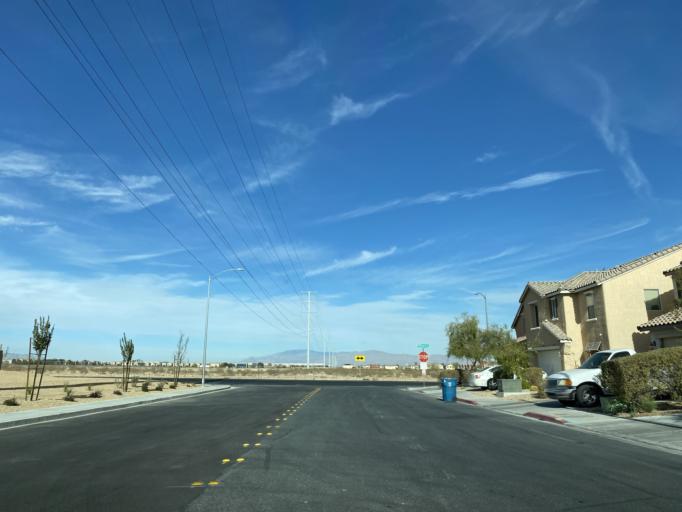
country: US
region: Nevada
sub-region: Clark County
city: Enterprise
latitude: 36.0417
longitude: -115.2124
